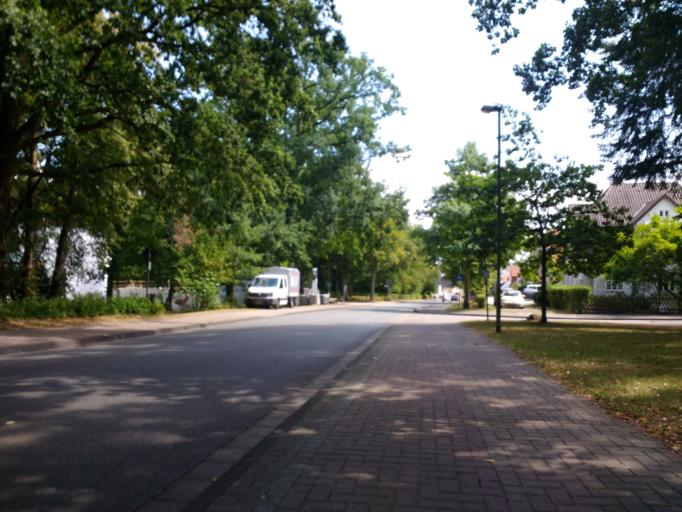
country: DE
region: Lower Saxony
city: Gifhorn
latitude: 52.4895
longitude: 10.5390
